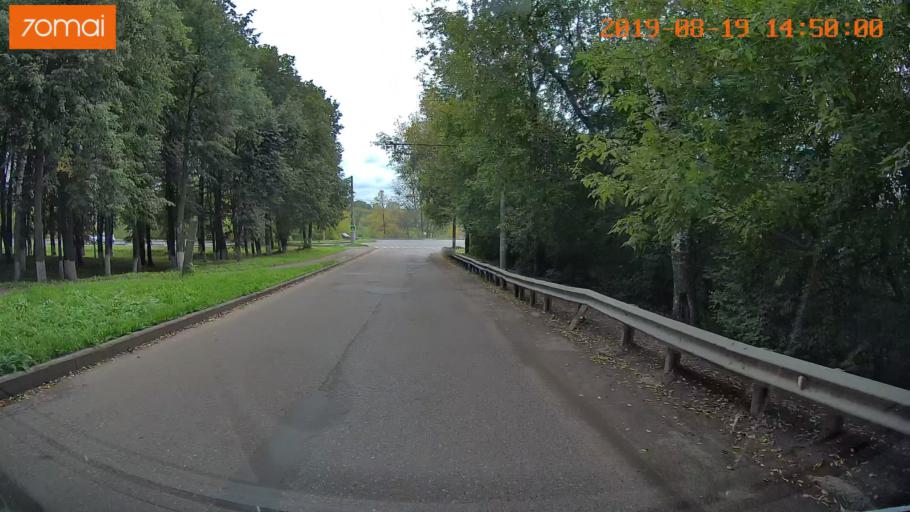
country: RU
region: Ivanovo
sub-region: Gorod Ivanovo
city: Ivanovo
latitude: 56.9943
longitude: 41.0189
